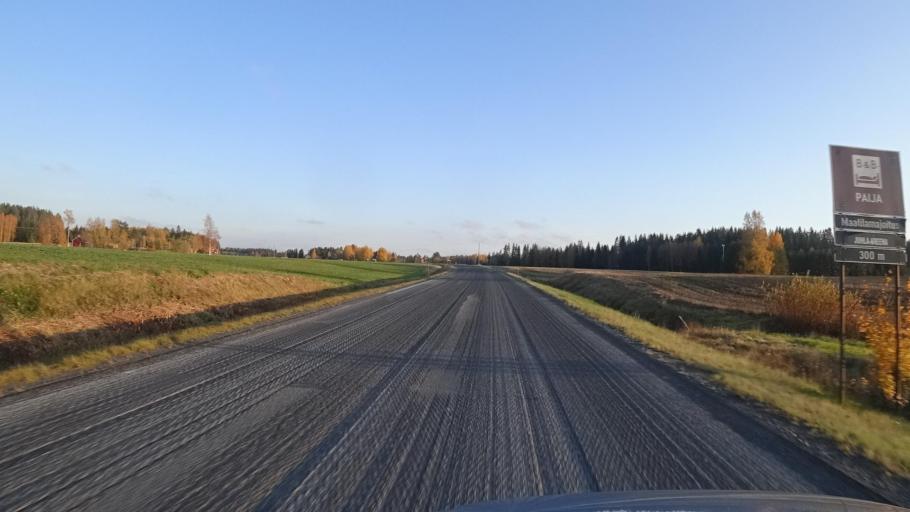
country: FI
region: Haeme
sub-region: Forssa
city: Ypaejae
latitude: 60.7815
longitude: 23.3076
